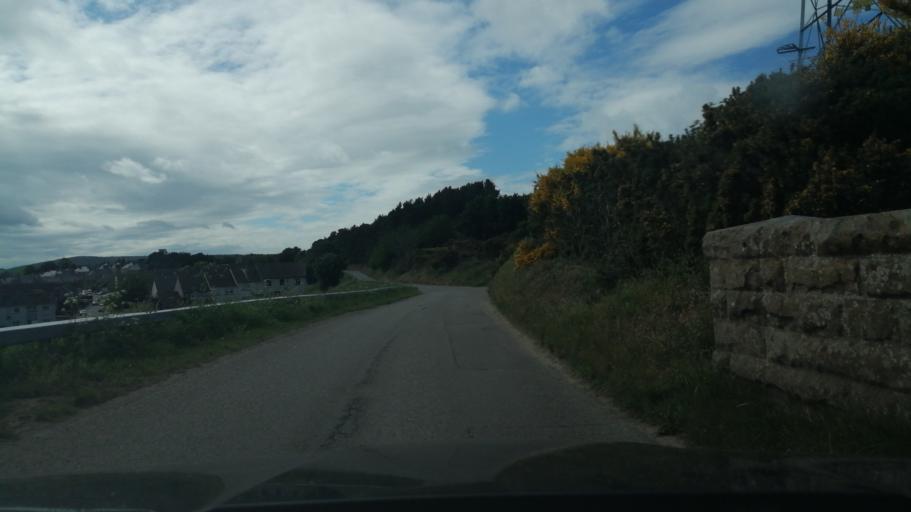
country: GB
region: Scotland
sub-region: Moray
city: Elgin
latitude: 57.6546
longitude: -3.2927
